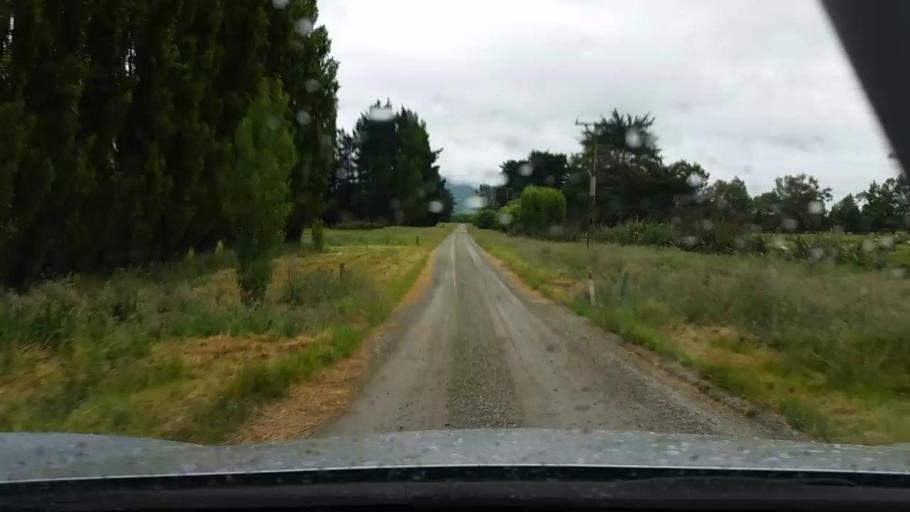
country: NZ
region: Southland
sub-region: Gore District
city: Gore
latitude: -46.0727
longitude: 168.9619
